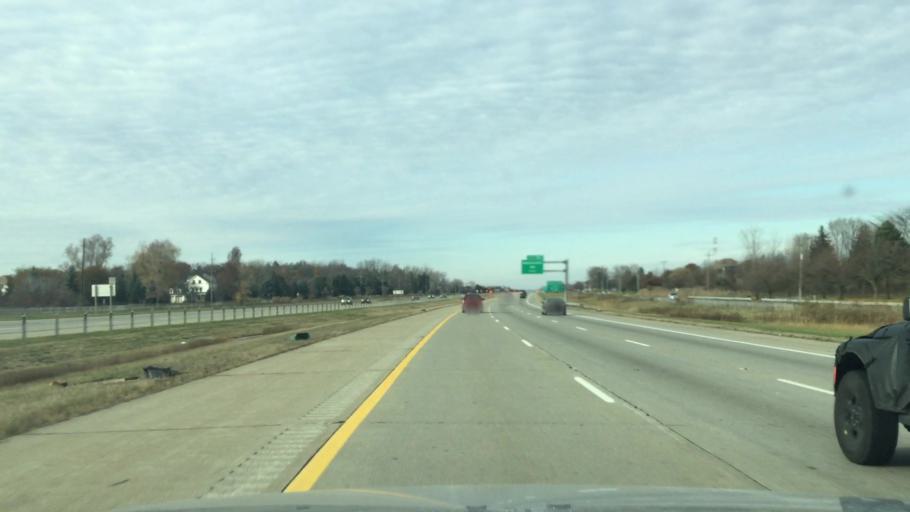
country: US
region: Michigan
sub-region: Wayne County
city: Belleville
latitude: 42.2205
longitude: -83.4570
